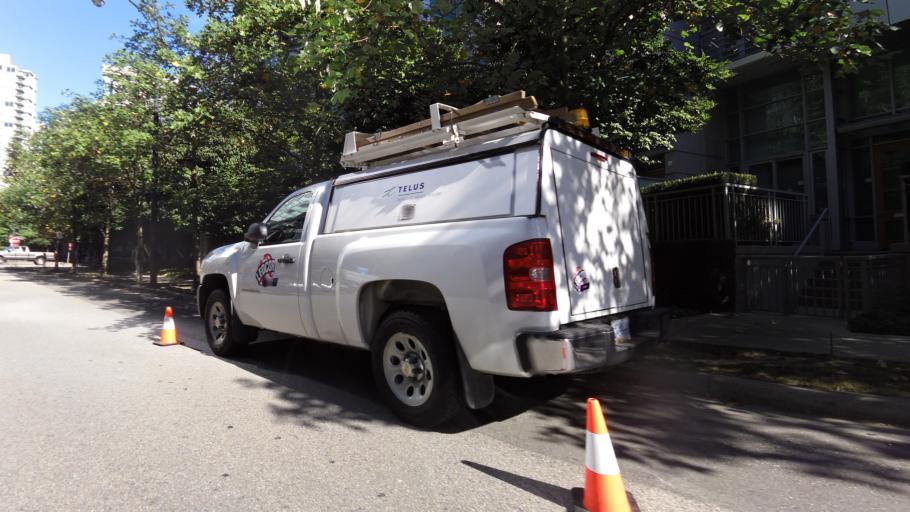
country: CA
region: British Columbia
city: West End
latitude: 49.2903
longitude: -123.1276
